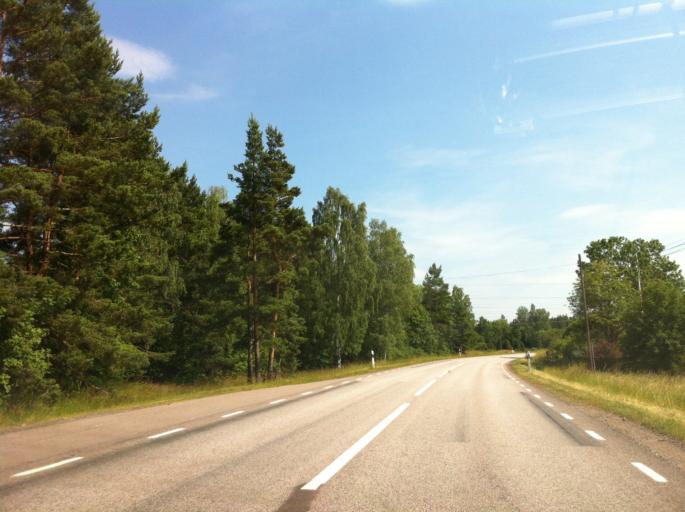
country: SE
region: Kalmar
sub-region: Nybro Kommun
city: Nybro
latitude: 56.7705
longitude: 15.8595
